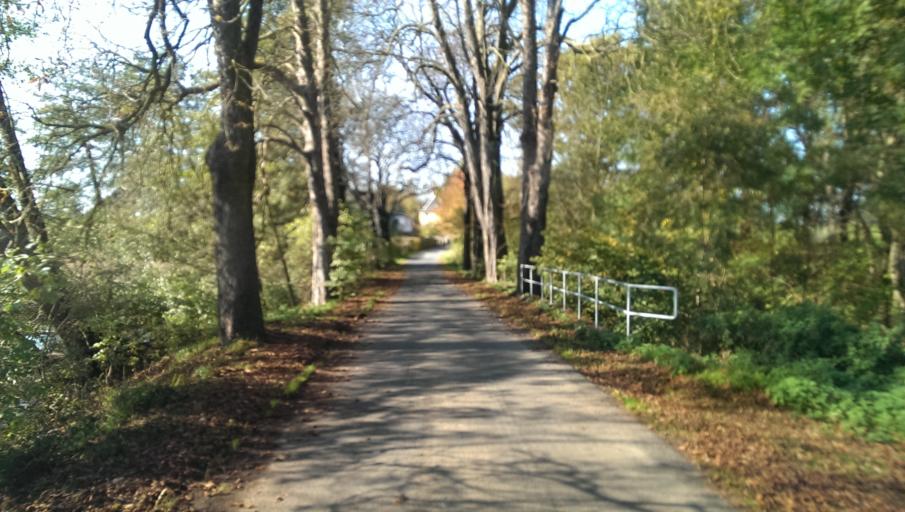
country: DE
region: Saxony
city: Kriebstein
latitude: 51.0422
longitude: 12.9849
